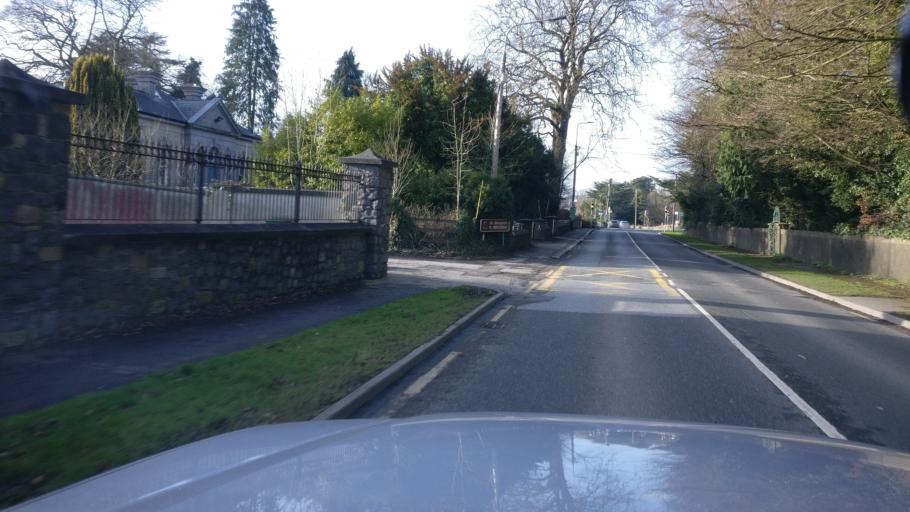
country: IE
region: Leinster
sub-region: Uibh Fhaili
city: Clara
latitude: 53.3390
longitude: -7.6078
